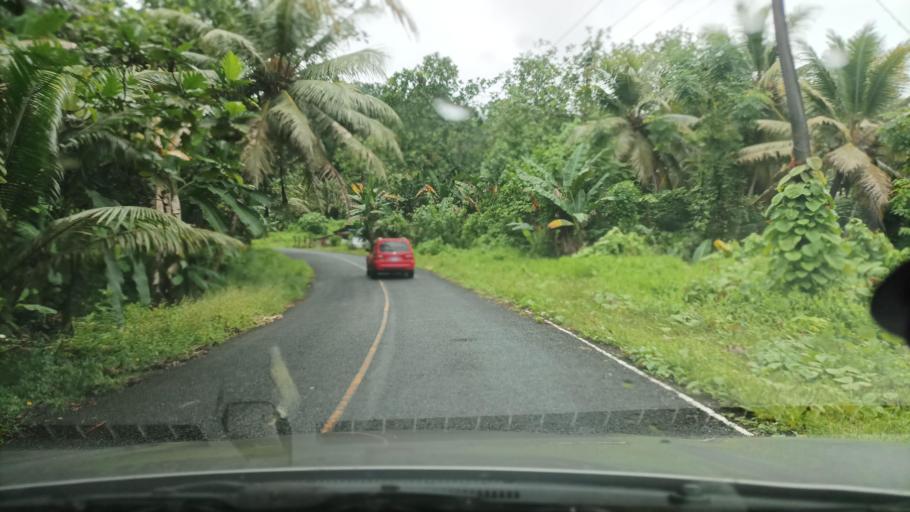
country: FM
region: Pohnpei
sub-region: Madolenihm Municipality
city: Madolenihm Municipality Government
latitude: 6.8051
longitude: 158.2673
